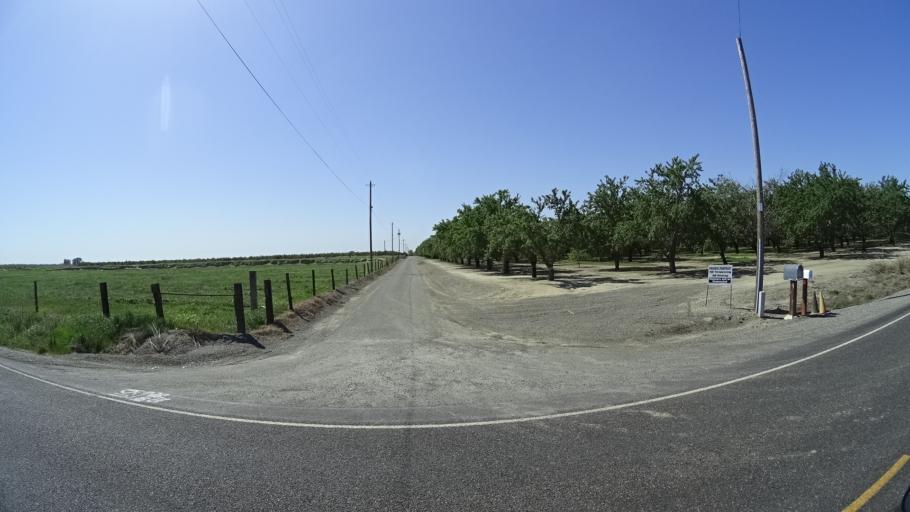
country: US
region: California
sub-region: Glenn County
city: Hamilton City
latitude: 39.7108
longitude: -122.0856
